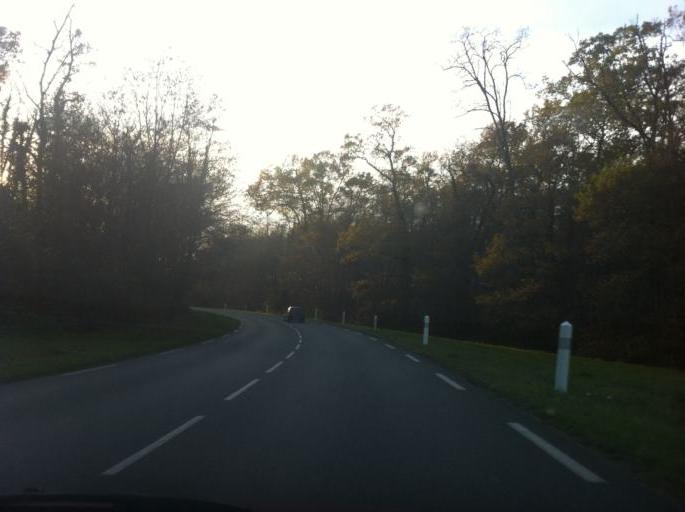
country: FR
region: Aquitaine
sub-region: Departement de la Dordogne
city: Tocane-Saint-Apre
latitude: 45.2512
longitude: 0.5176
